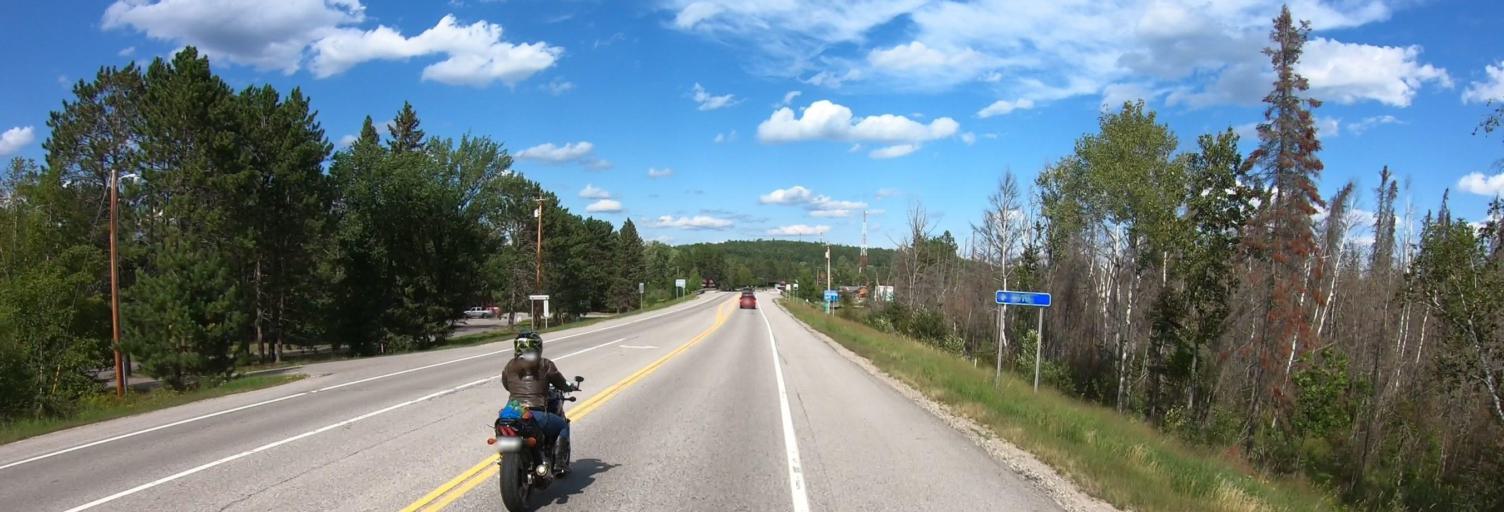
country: US
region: Minnesota
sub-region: Saint Louis County
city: Aurora
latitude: 47.8025
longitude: -92.2842
